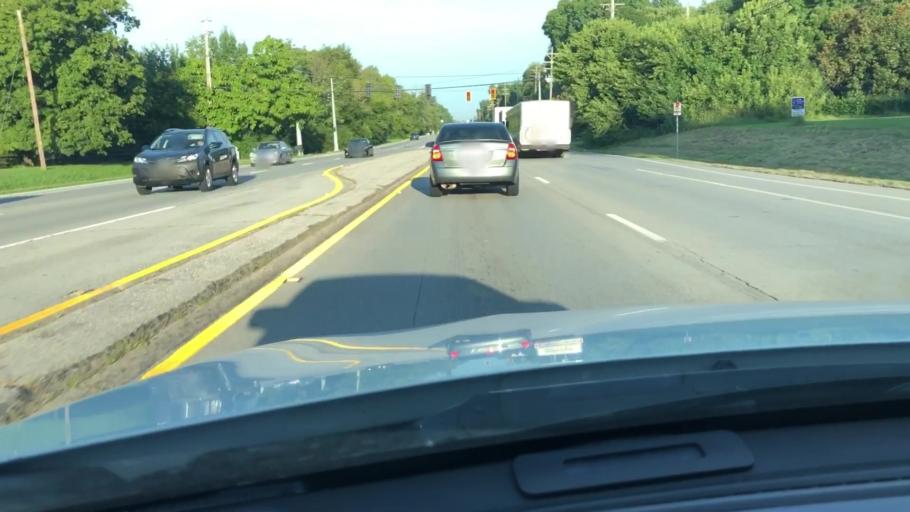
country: US
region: Kentucky
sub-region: Jefferson County
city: Saint Regis Park
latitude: 38.2189
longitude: -85.6058
